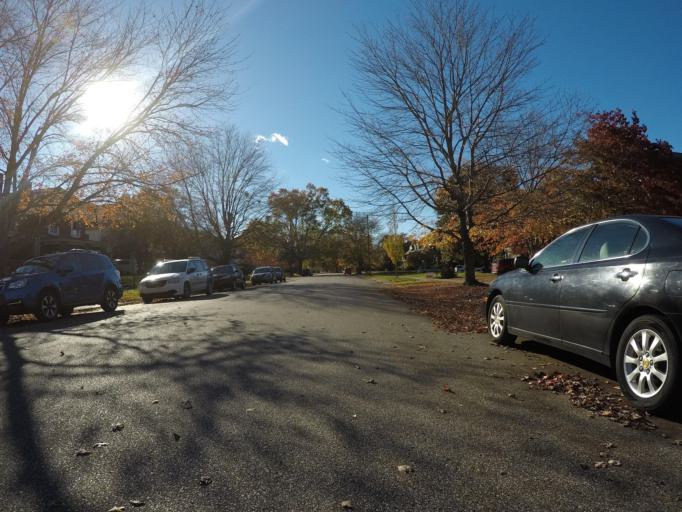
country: US
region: West Virginia
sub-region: Cabell County
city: Huntington
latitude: 38.4091
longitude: -82.4523
